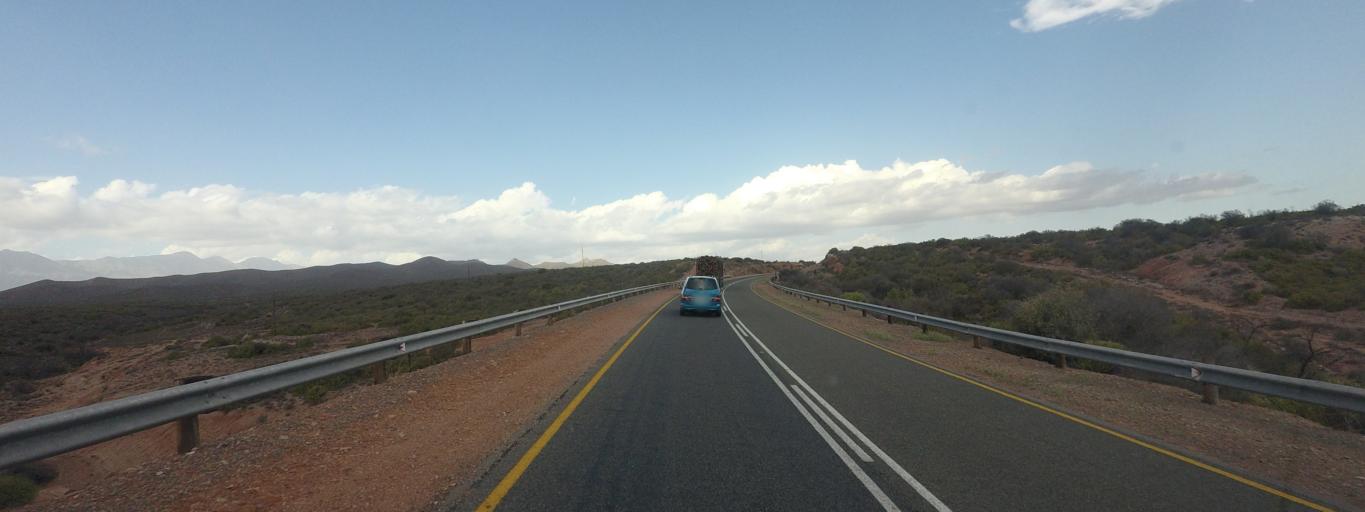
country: ZA
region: Western Cape
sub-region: Central Karoo District Municipality
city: Prince Albert
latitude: -33.5235
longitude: 21.7248
